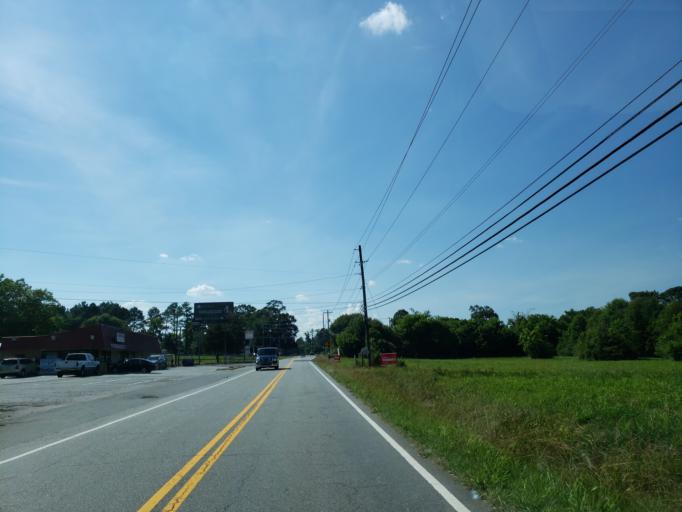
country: US
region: Georgia
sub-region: Cherokee County
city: Woodstock
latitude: 34.1133
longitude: -84.4572
